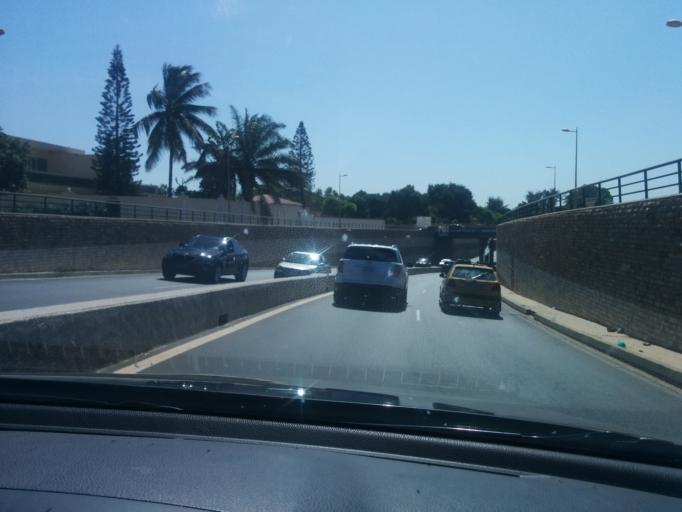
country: SN
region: Dakar
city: Mermoz Boabab
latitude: 14.6978
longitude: -17.4717
